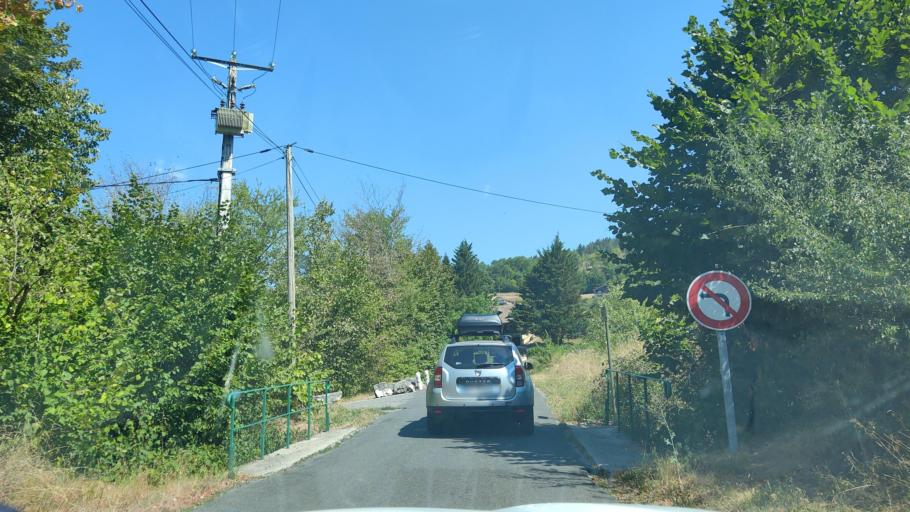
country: FR
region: Rhone-Alpes
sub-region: Departement de la Savoie
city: Novalaise
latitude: 45.6025
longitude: 5.7827
